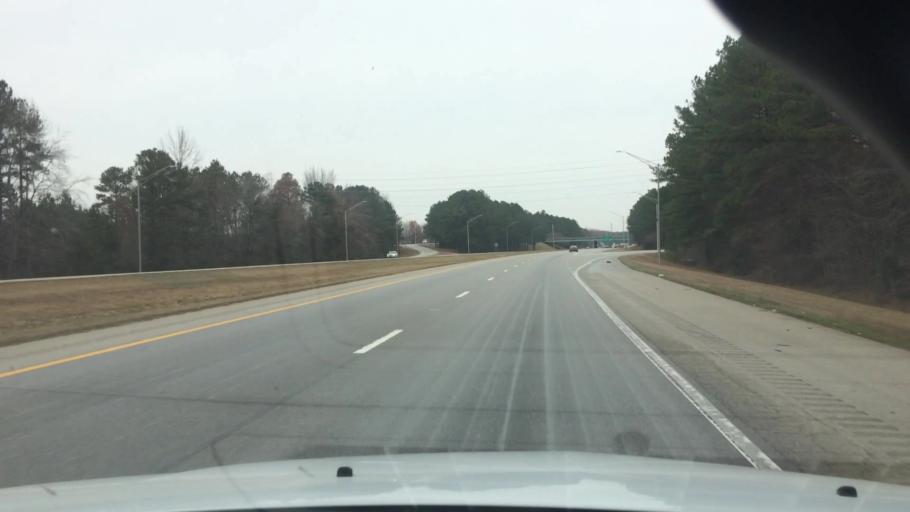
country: US
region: North Carolina
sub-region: Wilson County
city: Wilson
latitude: 35.7583
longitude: -78.0040
